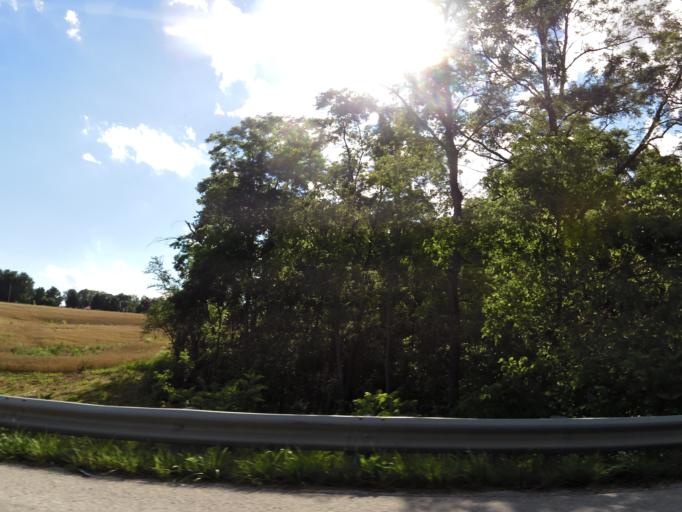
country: US
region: Missouri
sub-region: Marion County
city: Palmyra
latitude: 39.7716
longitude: -91.5189
